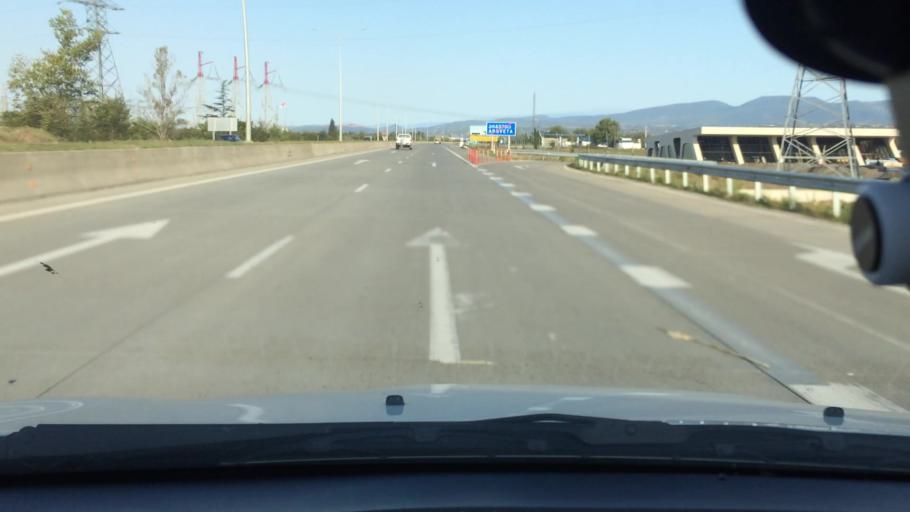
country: GE
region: Imereti
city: Zestap'oni
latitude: 42.1461
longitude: 42.9662
